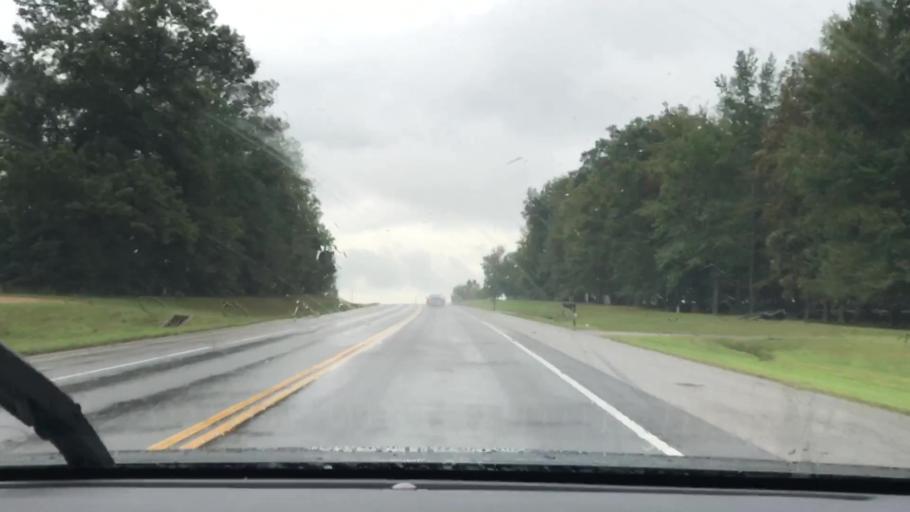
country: US
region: Tennessee
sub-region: Macon County
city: Lafayette
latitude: 36.5305
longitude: -86.0732
